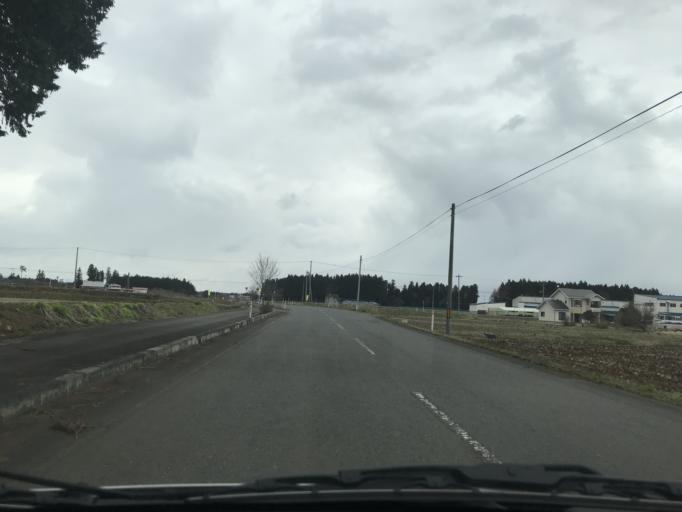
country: JP
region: Iwate
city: Mizusawa
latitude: 39.0846
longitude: 141.0799
